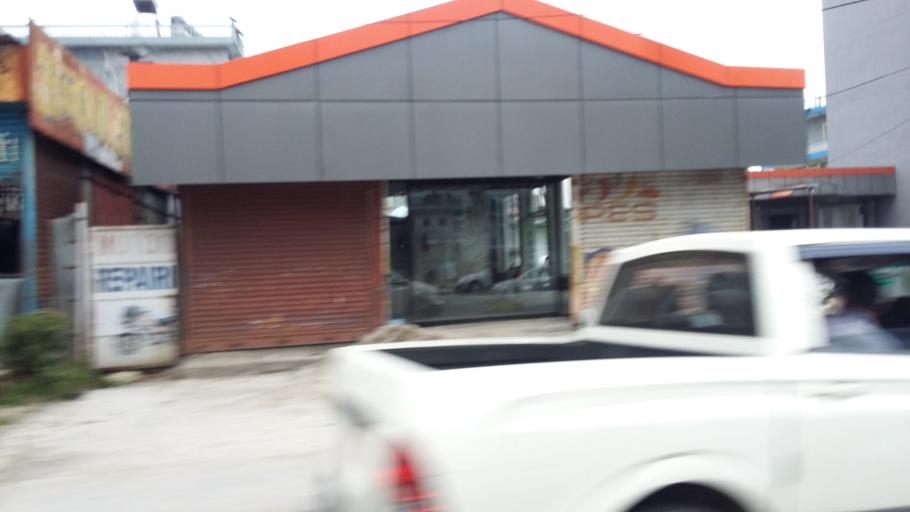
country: NP
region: Western Region
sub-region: Gandaki Zone
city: Pokhara
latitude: 28.2140
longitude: 83.9857
